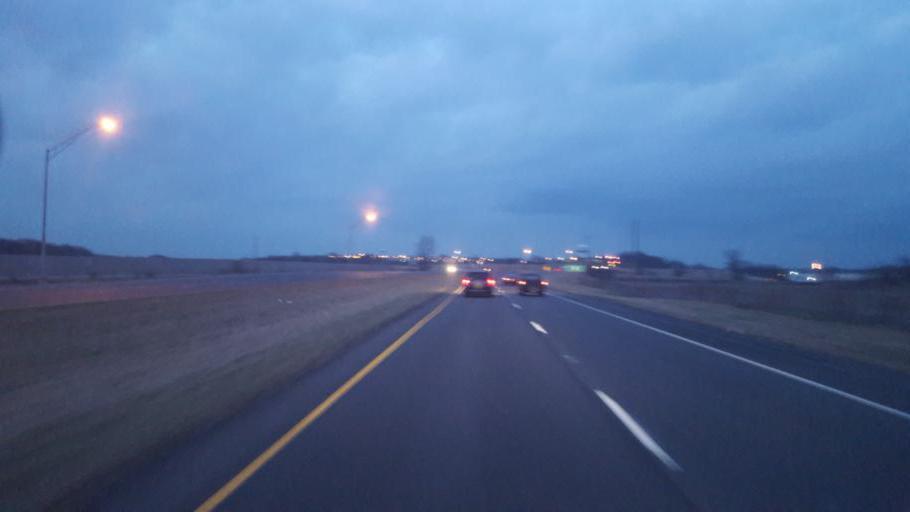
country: US
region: Ohio
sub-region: Ross County
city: Chillicothe
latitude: 39.3837
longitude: -82.9726
